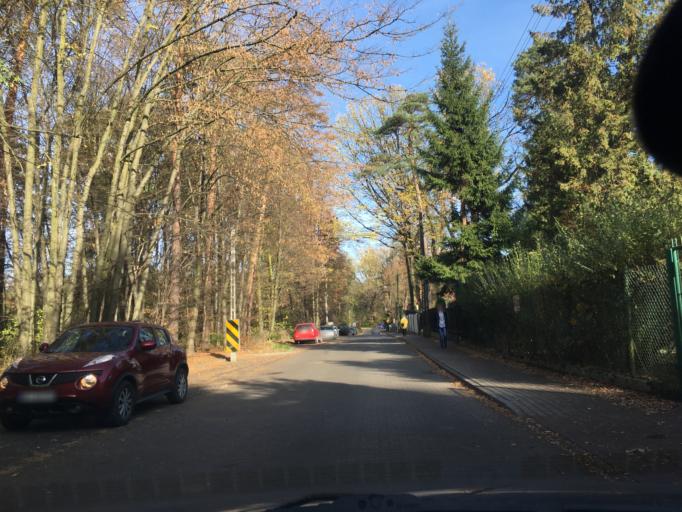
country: PL
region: Masovian Voivodeship
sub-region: Powiat piaseczynski
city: Piaseczno
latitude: 52.0587
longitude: 21.0100
